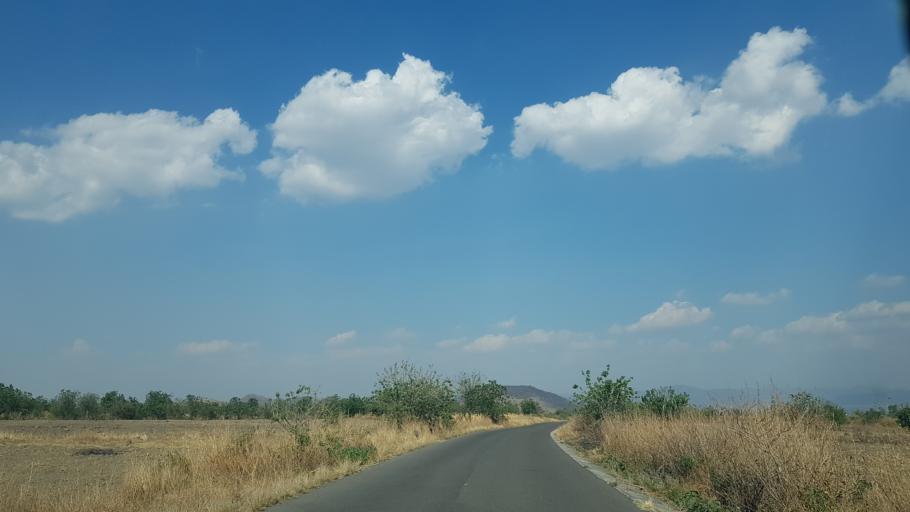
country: MX
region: Puebla
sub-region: Atlixco
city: Colonia Agricola de Ocotepec (Colonia San Jose)
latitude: 18.9234
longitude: -98.5071
